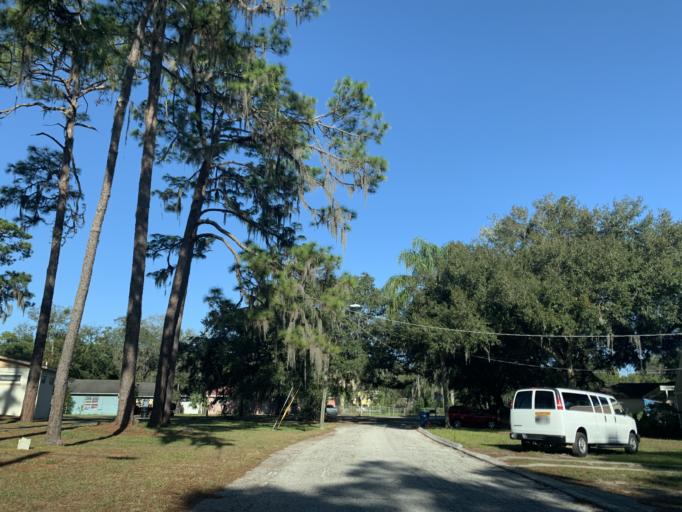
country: US
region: Florida
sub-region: Hillsborough County
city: Temple Terrace
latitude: 28.0225
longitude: -82.4108
